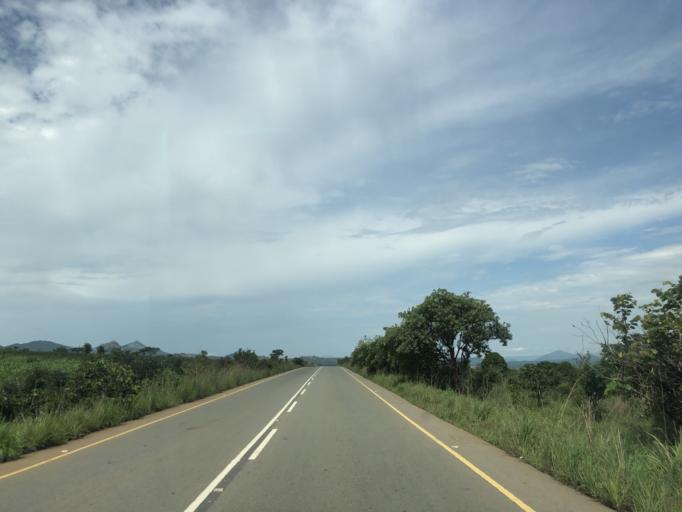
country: AO
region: Cuanza Sul
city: Quibala
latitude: -10.7331
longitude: 15.0191
